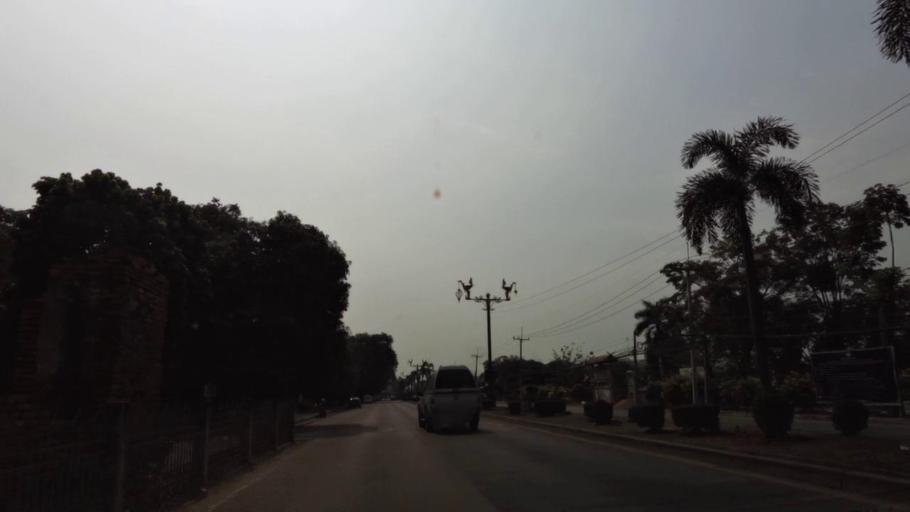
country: TH
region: Phra Nakhon Si Ayutthaya
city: Phra Nakhon Si Ayutthaya
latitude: 14.3486
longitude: 100.5603
